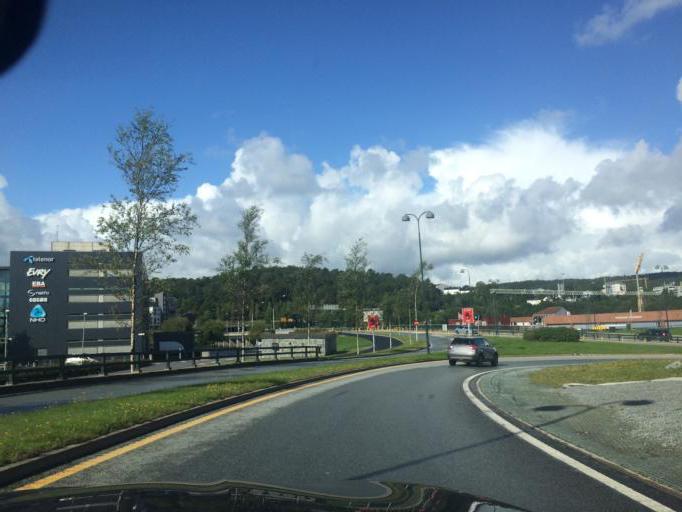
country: NO
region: Vest-Agder
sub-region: Kristiansand
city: Kristiansand
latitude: 58.1551
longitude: 8.0025
